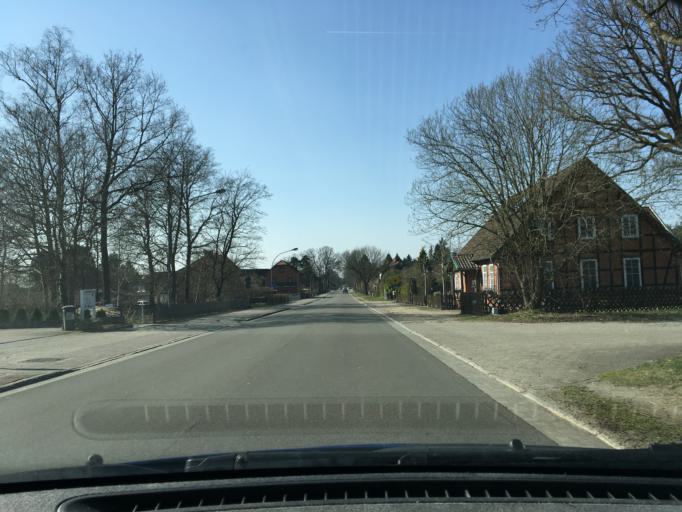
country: DE
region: Lower Saxony
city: Hermannsburg
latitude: 52.8279
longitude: 10.1058
